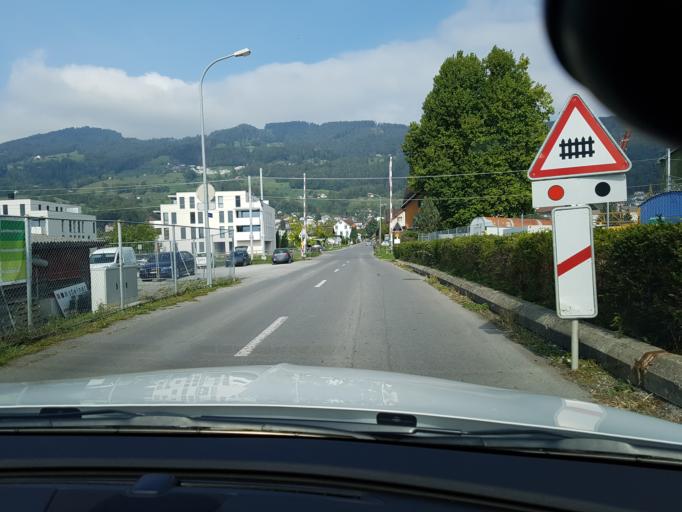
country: CH
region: Saint Gallen
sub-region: Wahlkreis Rheintal
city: Rebstein
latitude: 47.3926
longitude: 9.5885
